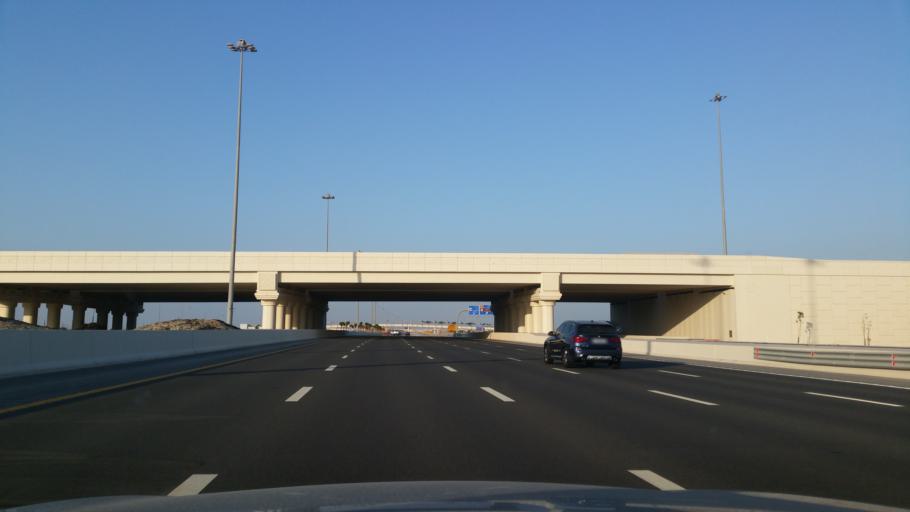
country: QA
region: Al Khawr
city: Al Khawr
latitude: 25.6403
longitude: 51.4927
